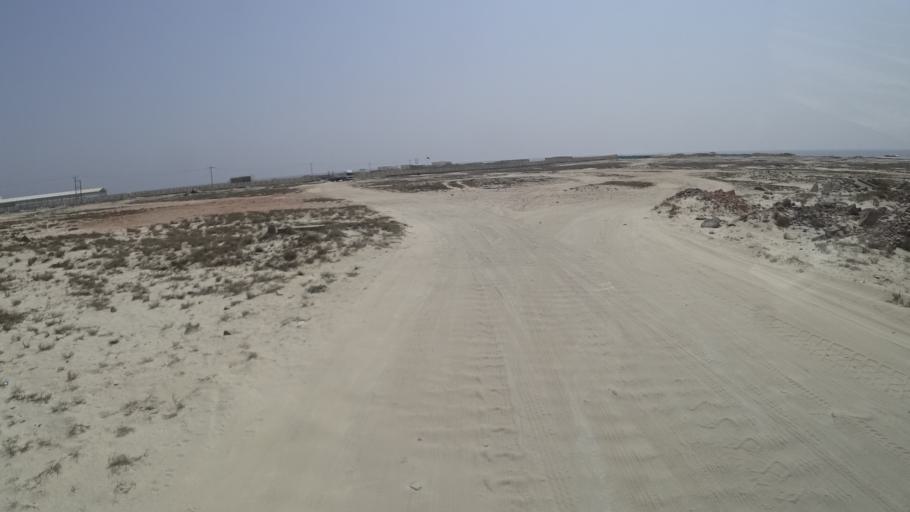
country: OM
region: Zufar
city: Salalah
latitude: 16.9726
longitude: 54.7001
